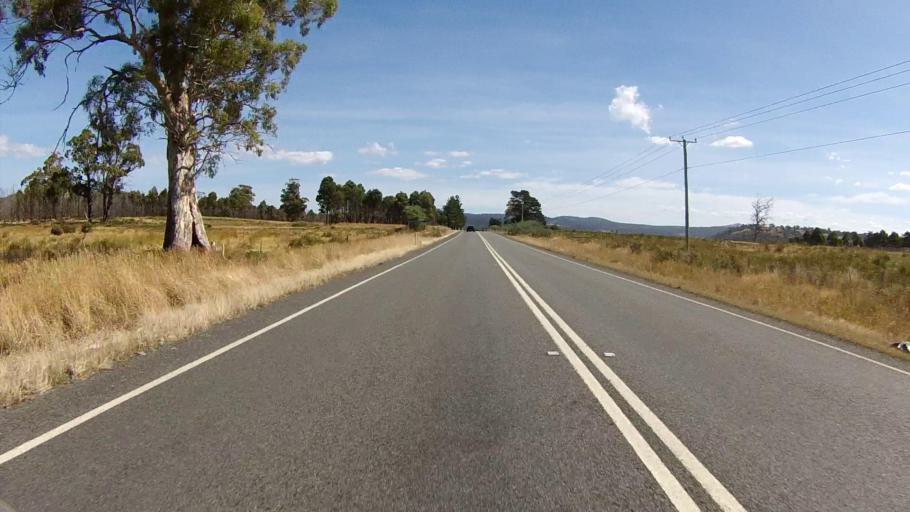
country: AU
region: Tasmania
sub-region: Sorell
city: Sorell
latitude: -42.6024
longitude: 147.7538
